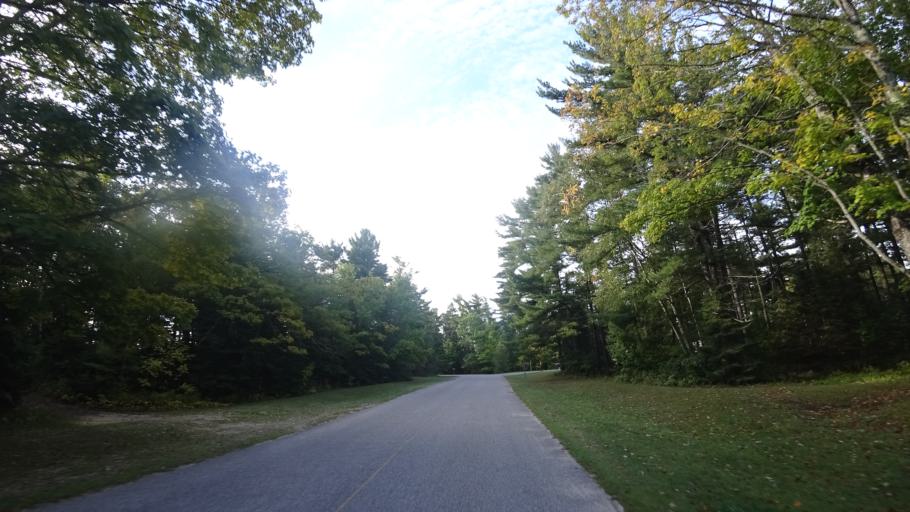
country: US
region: Michigan
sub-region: Mackinac County
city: Saint Ignace
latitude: 45.7441
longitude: -84.8995
